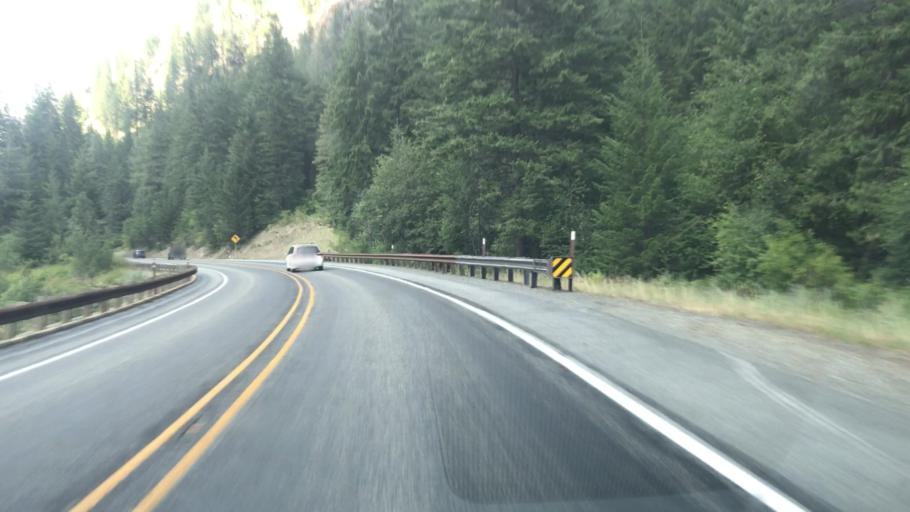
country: US
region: Washington
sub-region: Chelan County
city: Leavenworth
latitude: 47.6399
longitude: -120.7200
